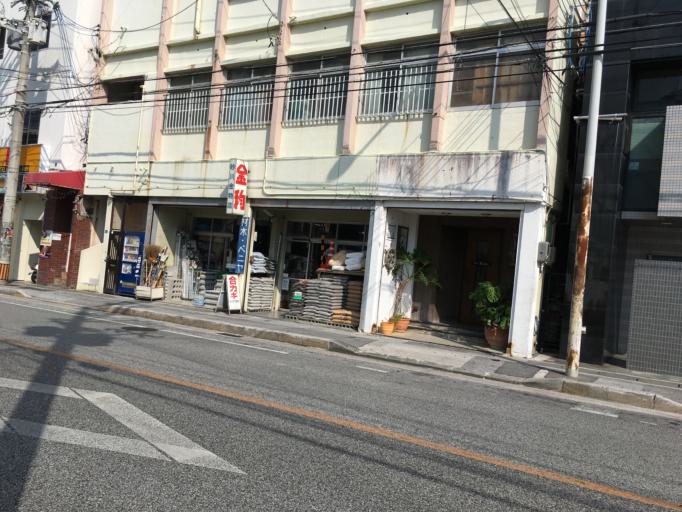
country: JP
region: Okinawa
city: Naha-shi
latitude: 26.2198
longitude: 127.6757
